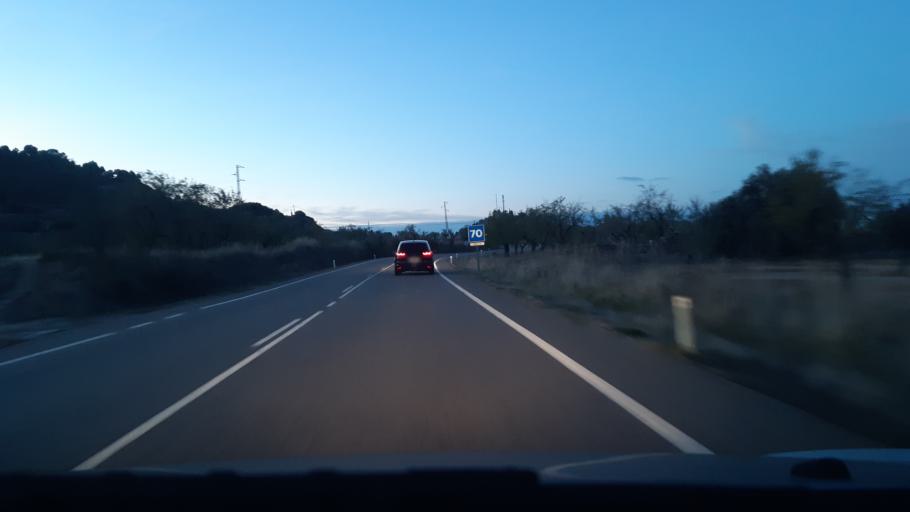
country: ES
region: Aragon
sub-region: Provincia de Teruel
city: Calaceite
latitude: 41.0075
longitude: 0.1914
